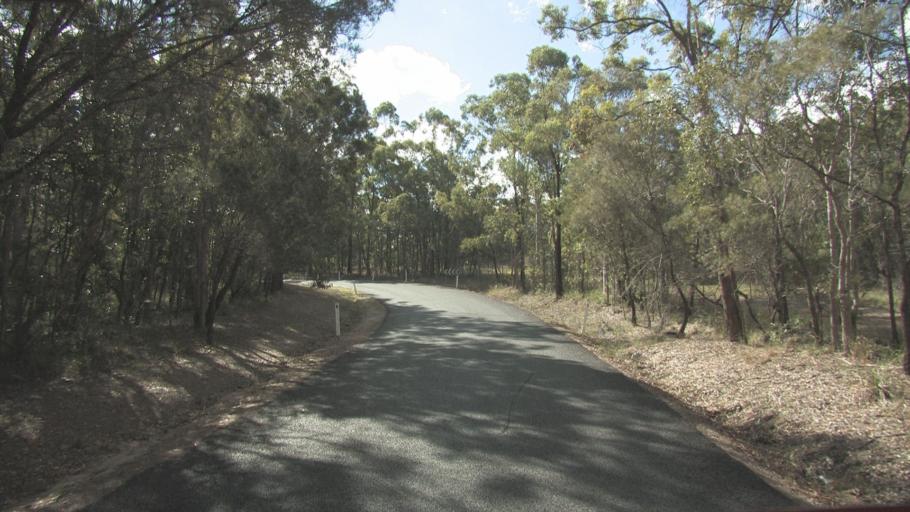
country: AU
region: Queensland
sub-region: Logan
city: Beenleigh
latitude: -27.6525
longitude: 153.2302
